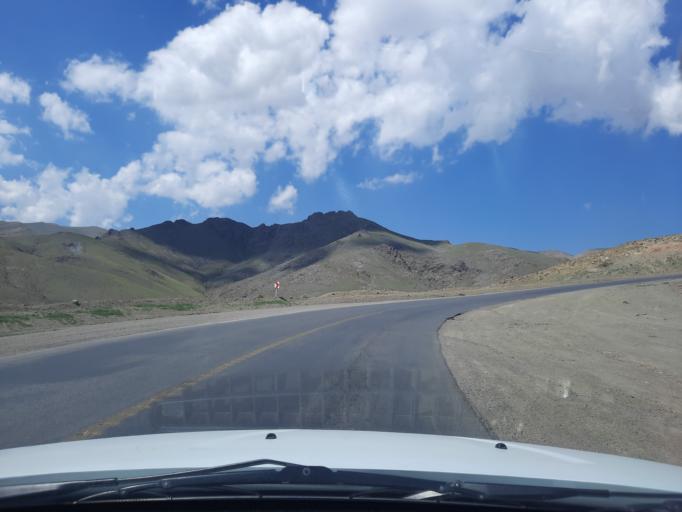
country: IR
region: Qazvin
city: Qazvin
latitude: 36.3551
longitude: 50.1868
